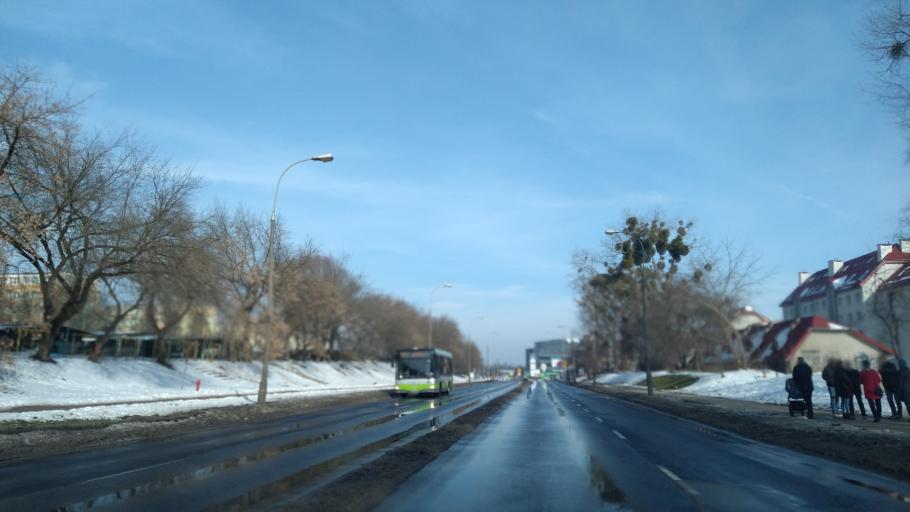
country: PL
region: Warmian-Masurian Voivodeship
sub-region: Powiat olsztynski
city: Olsztyn
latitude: 53.7671
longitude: 20.5055
